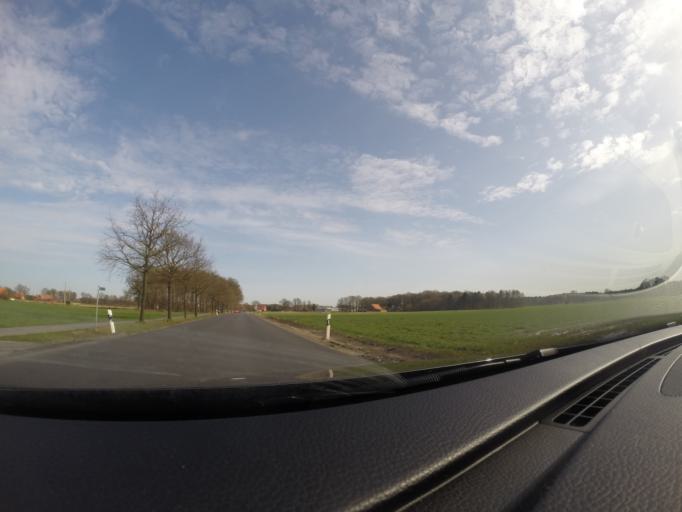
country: DE
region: North Rhine-Westphalia
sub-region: Regierungsbezirk Munster
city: Legden
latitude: 52.0488
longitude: 7.0703
